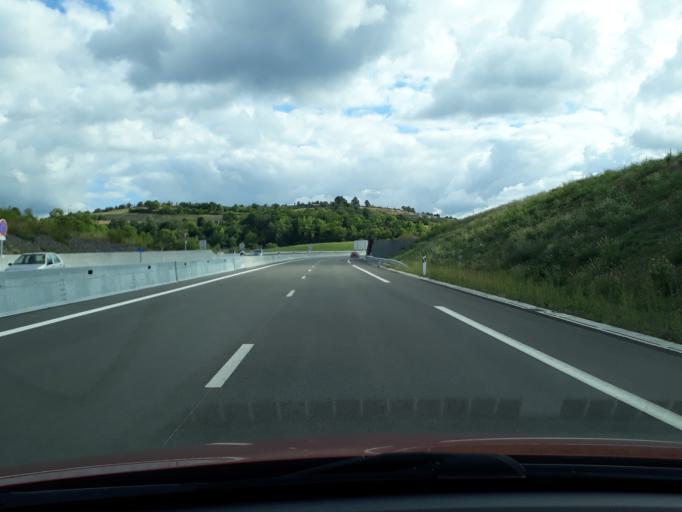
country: FR
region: Auvergne
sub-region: Departement de la Haute-Loire
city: Le Puy-en-Velay
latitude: 45.0321
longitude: 3.9062
